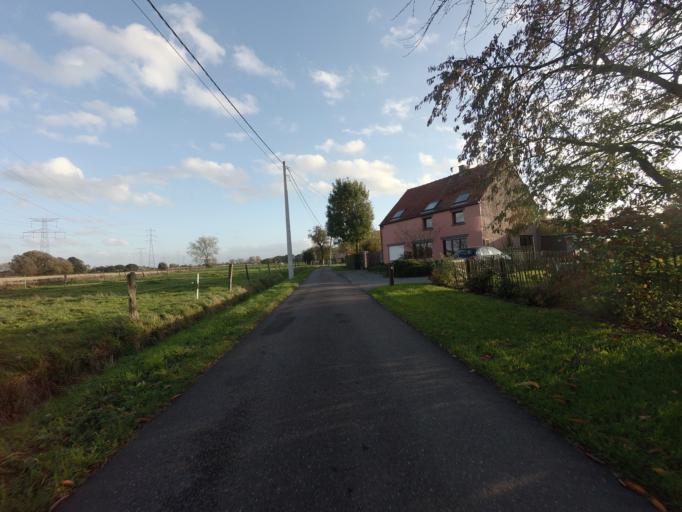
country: BE
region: Flanders
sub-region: Provincie Vlaams-Brabant
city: Zemst
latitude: 50.9762
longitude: 4.4163
